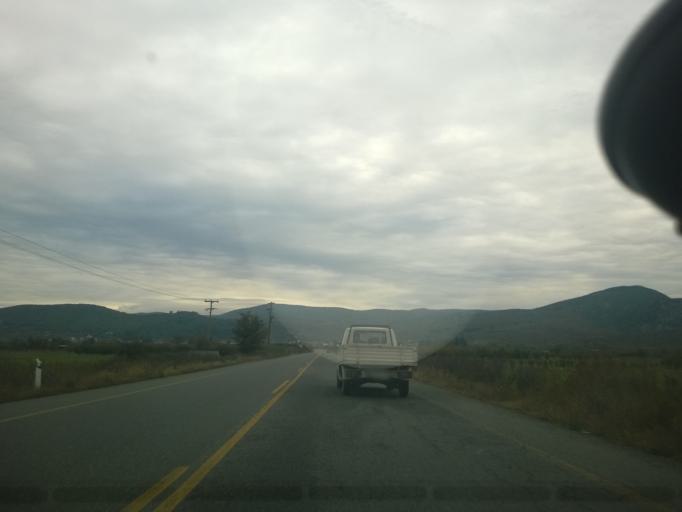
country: GR
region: Central Macedonia
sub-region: Nomos Pellis
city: Apsalos
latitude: 40.9047
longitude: 22.0666
